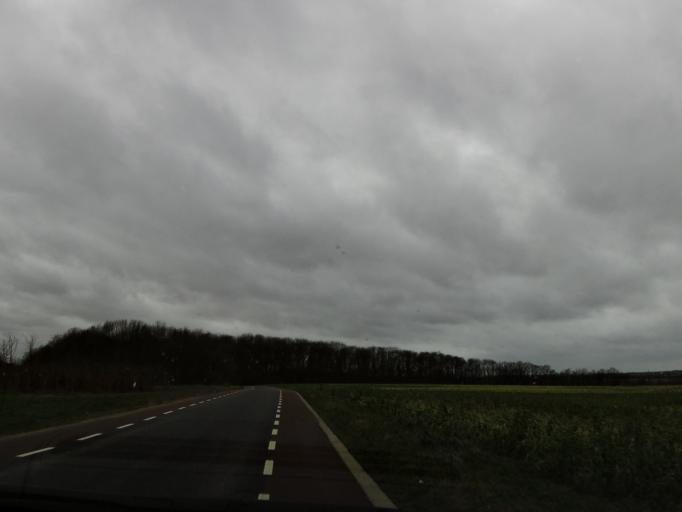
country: NL
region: Limburg
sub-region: Eijsden-Margraten
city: Margraten
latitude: 50.8113
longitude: 5.8104
